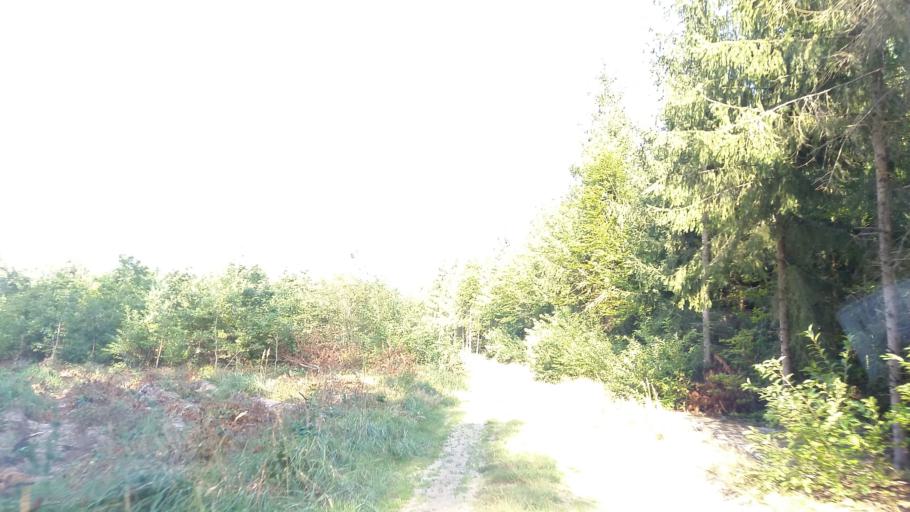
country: PL
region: West Pomeranian Voivodeship
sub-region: Powiat choszczenski
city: Choszczno
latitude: 53.2398
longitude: 15.4244
